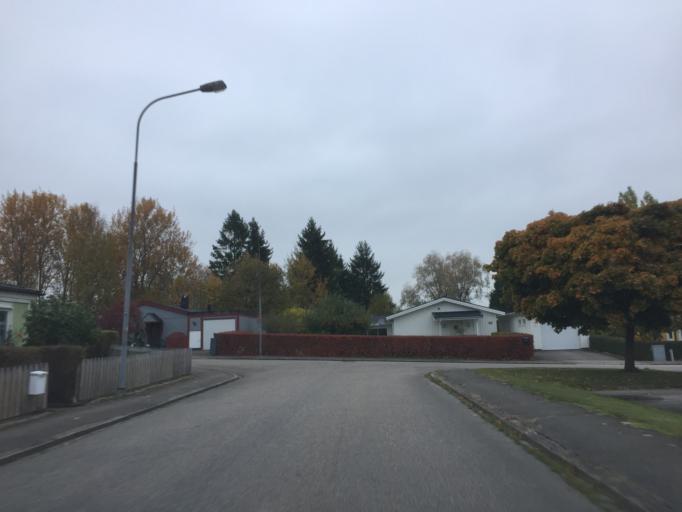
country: SE
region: Vaestra Goetaland
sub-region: Trollhattan
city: Trollhattan
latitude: 58.2926
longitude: 12.3298
